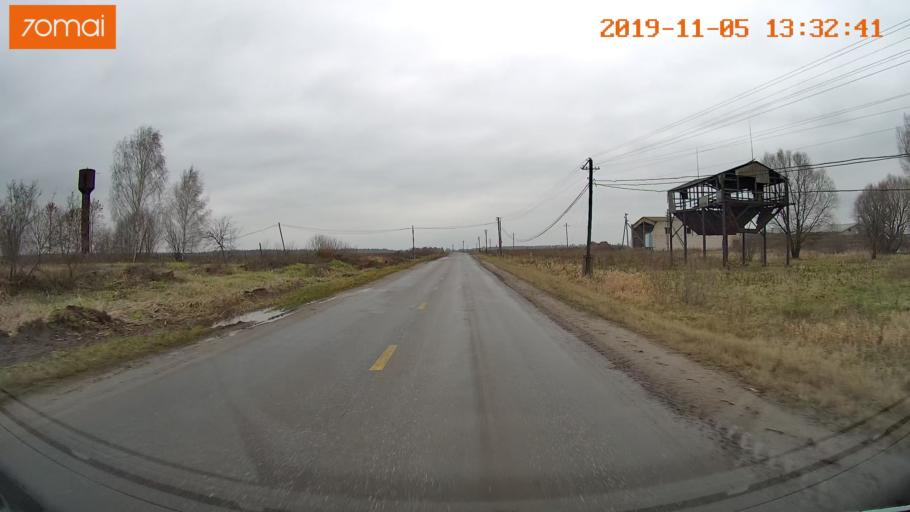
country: RU
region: Ivanovo
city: Shuya
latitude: 56.8853
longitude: 41.3970
